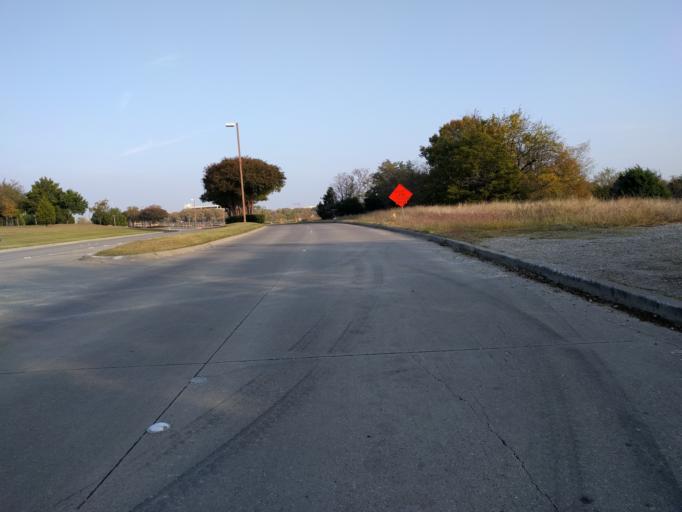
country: US
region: Texas
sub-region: Collin County
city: Plano
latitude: 32.9877
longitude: -96.7038
